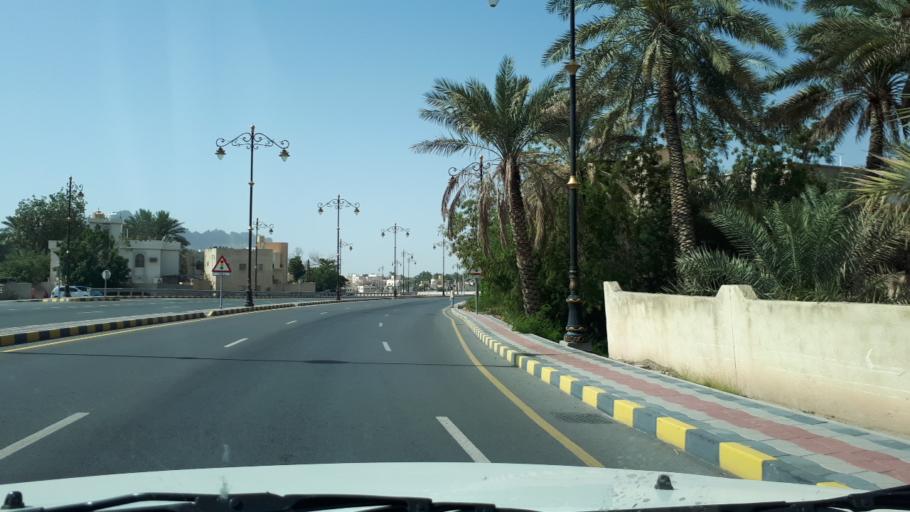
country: OM
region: Muhafazat ad Dakhiliyah
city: Nizwa
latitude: 22.9333
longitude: 57.5351
